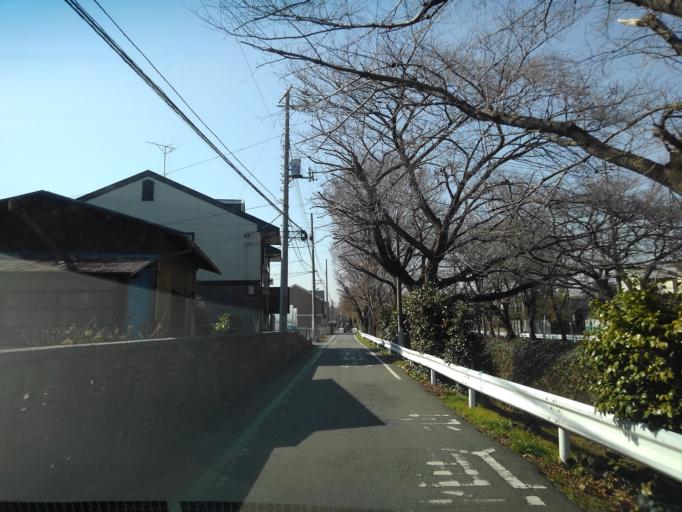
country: JP
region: Saitama
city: Tokorozawa
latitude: 35.7957
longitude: 139.4843
